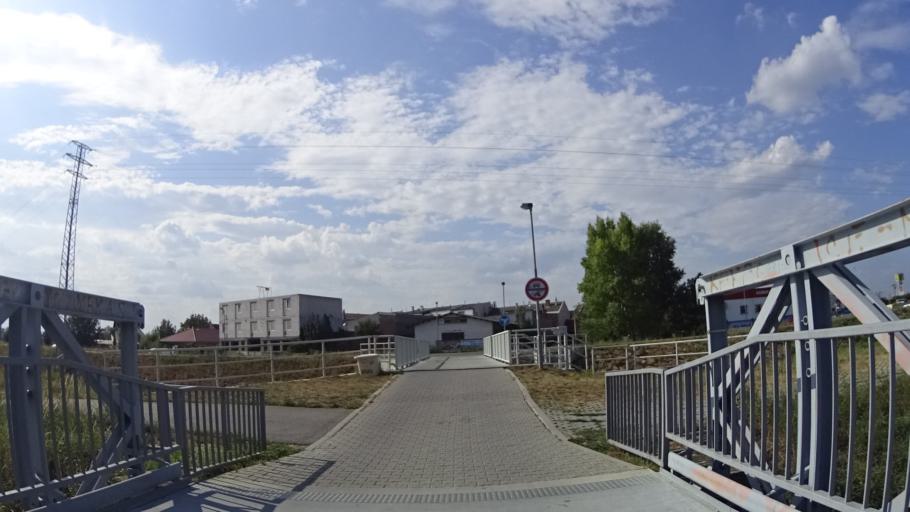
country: CZ
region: Zlin
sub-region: Okres Uherske Hradiste
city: Uherske Hradiste
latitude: 49.0741
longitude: 17.4544
